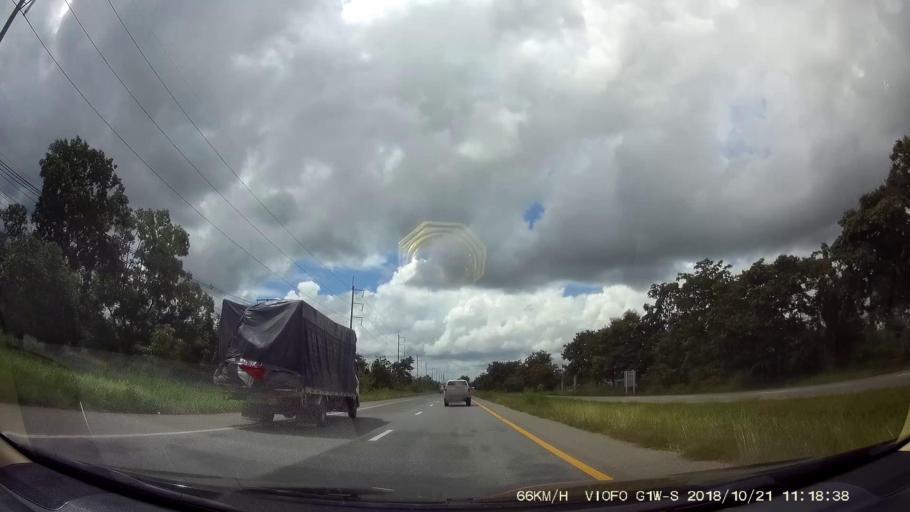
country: TH
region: Chaiyaphum
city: Chaiyaphum
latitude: 15.8761
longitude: 102.0941
